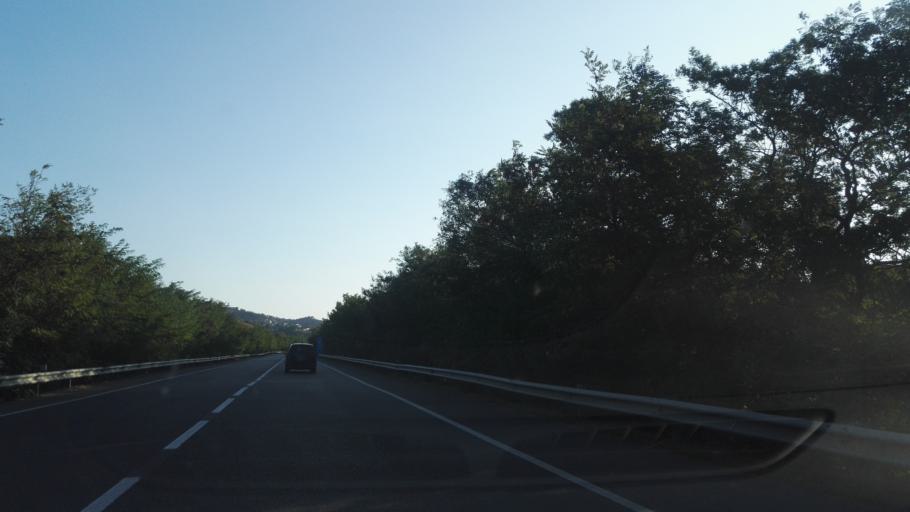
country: IT
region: Calabria
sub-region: Provincia di Catanzaro
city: Montepaone Lido
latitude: 38.7315
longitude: 16.5403
